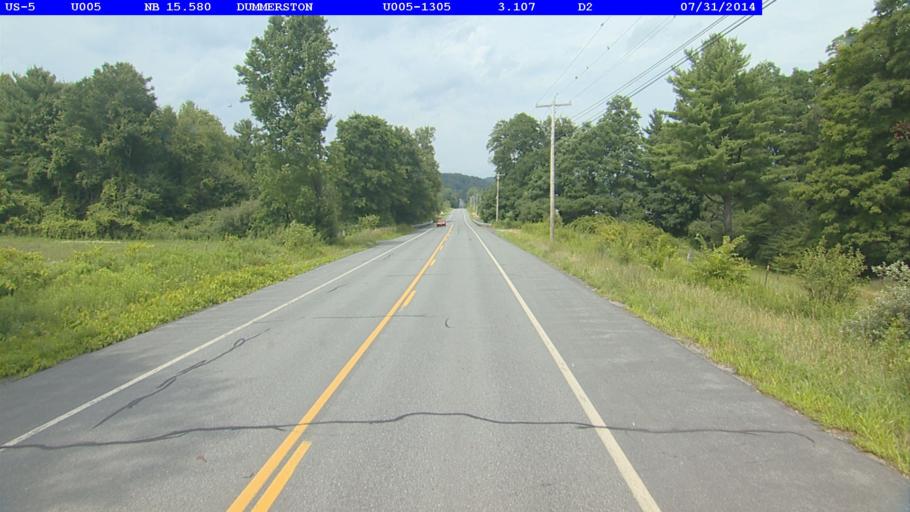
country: US
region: New Hampshire
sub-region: Cheshire County
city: Chesterfield
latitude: 42.9373
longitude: -72.5353
